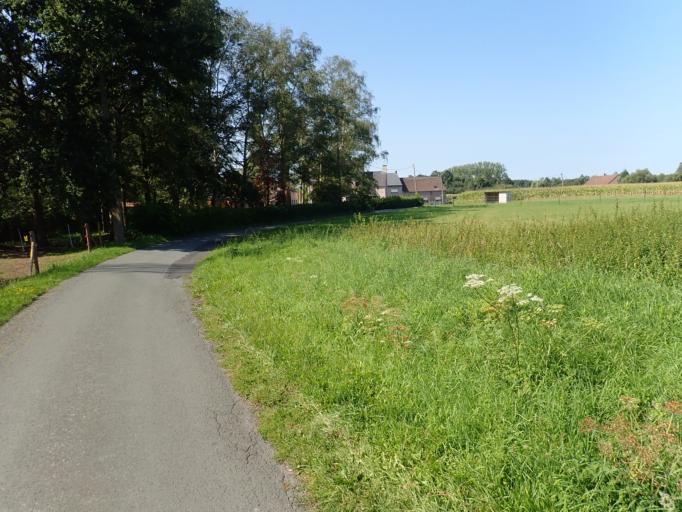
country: BE
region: Flanders
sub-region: Provincie Antwerpen
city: Puurs
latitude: 51.0397
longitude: 4.2908
